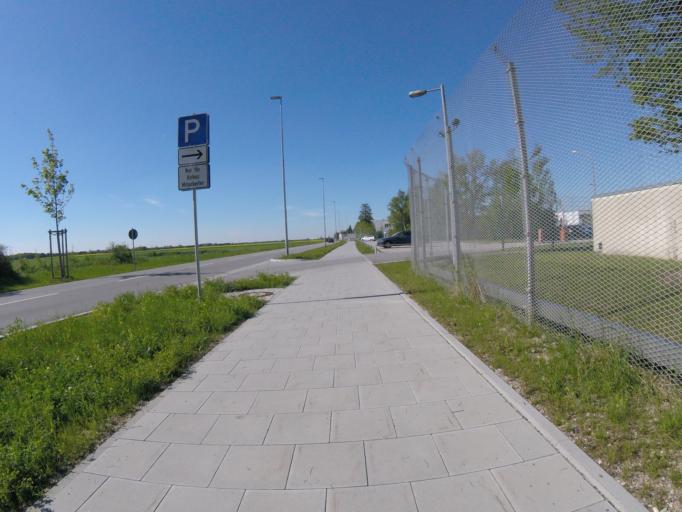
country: DE
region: Bavaria
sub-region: Upper Bavaria
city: Ottobrunn
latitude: 48.0456
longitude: 11.6531
